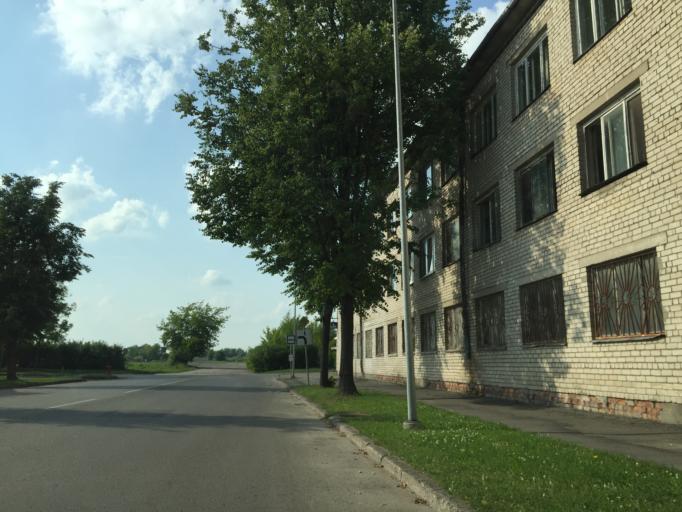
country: LV
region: Jelgava
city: Jelgava
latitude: 56.6608
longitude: 23.7141
